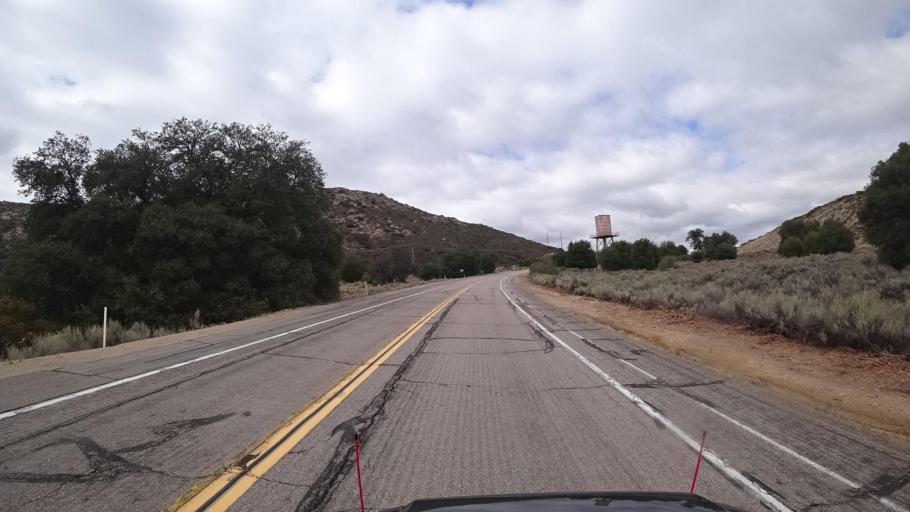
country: US
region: California
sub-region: San Diego County
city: Campo
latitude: 32.7177
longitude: -116.4730
